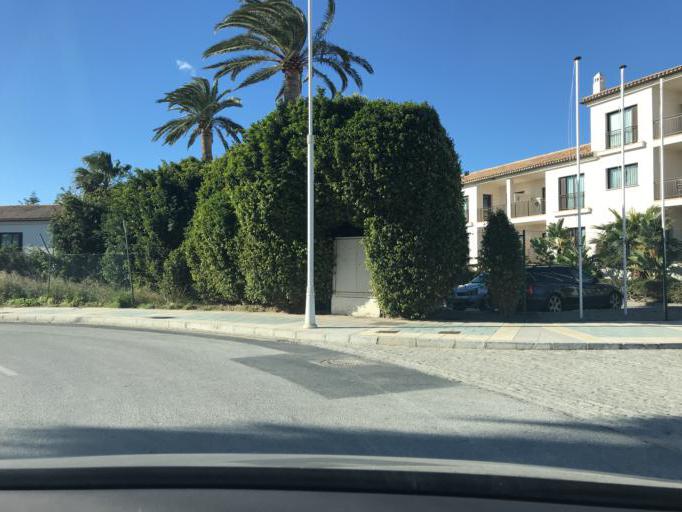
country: ES
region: Andalusia
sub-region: Provincia de Granada
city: Salobrena
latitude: 36.7209
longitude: -3.5629
